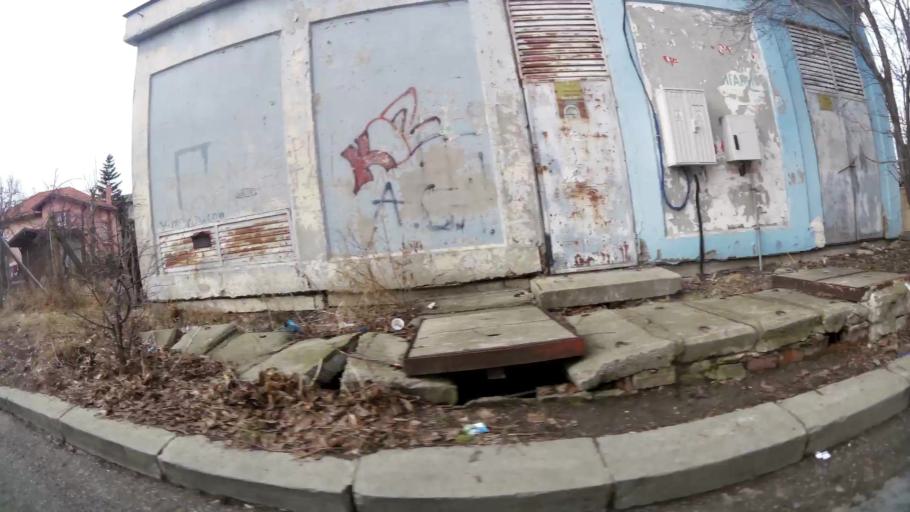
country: BG
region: Sofiya
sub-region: Obshtina Bozhurishte
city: Bozhurishte
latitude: 42.7461
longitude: 23.2677
